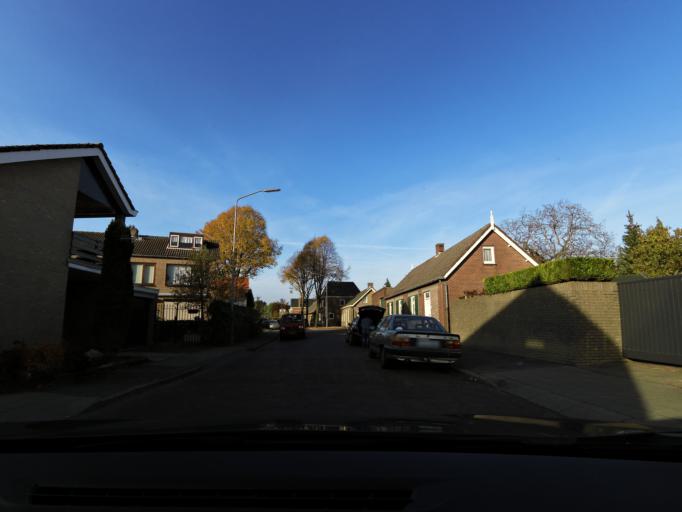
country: NL
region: North Brabant
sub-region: Gemeente Made en Drimmelen
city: Made
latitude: 51.6833
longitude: 4.7960
